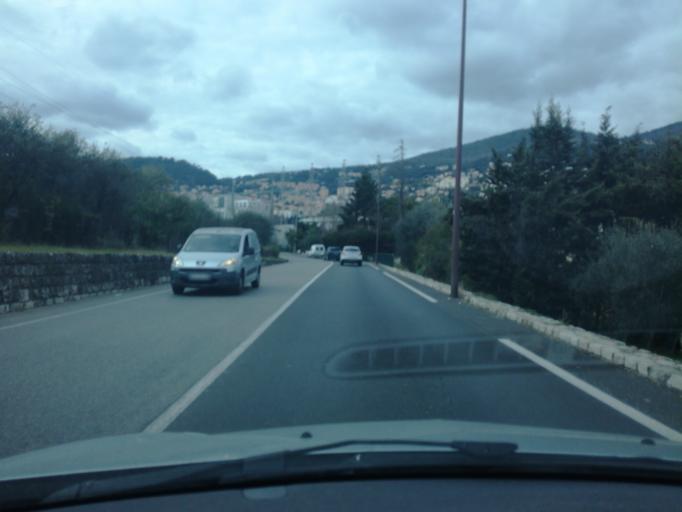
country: FR
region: Provence-Alpes-Cote d'Azur
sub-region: Departement des Alpes-Maritimes
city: Grasse
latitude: 43.6550
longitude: 6.9424
